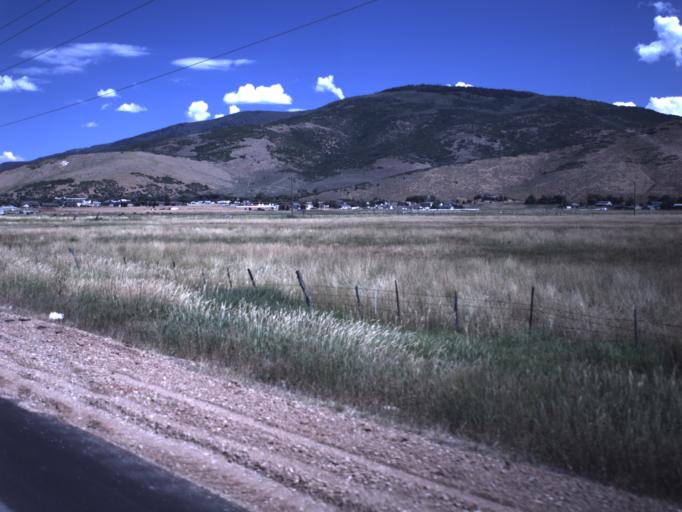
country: US
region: Utah
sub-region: Summit County
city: Francis
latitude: 40.6235
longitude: -111.2807
